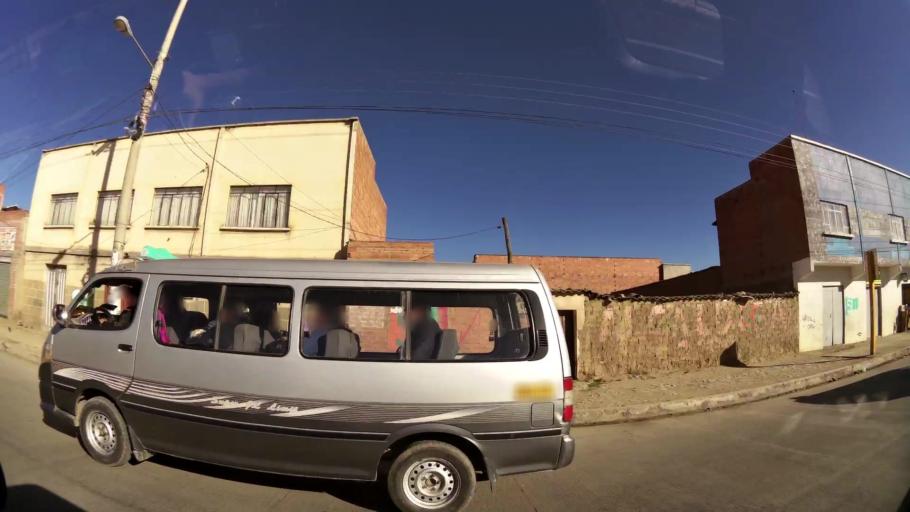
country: BO
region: La Paz
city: La Paz
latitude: -16.5253
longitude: -68.1594
